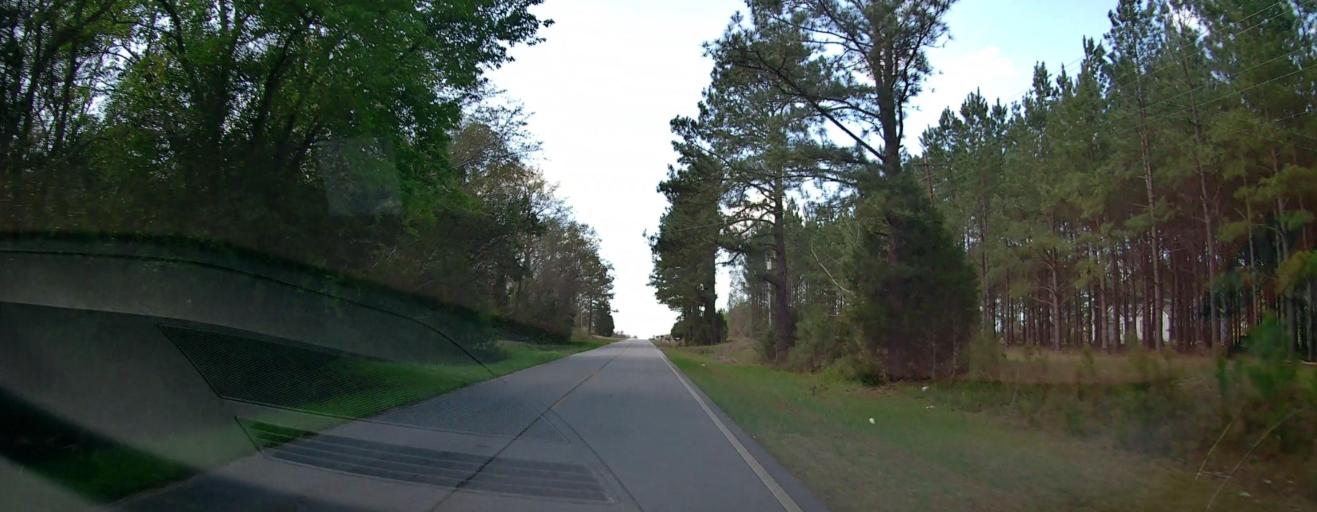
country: US
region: Georgia
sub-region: Wilkinson County
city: Gordon
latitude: 32.8286
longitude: -83.4263
